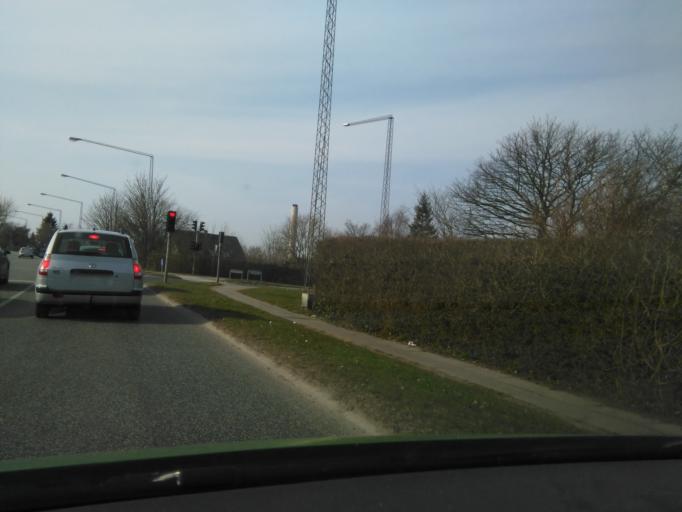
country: DK
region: Central Jutland
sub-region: Arhus Kommune
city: Arhus
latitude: 56.1965
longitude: 10.2186
